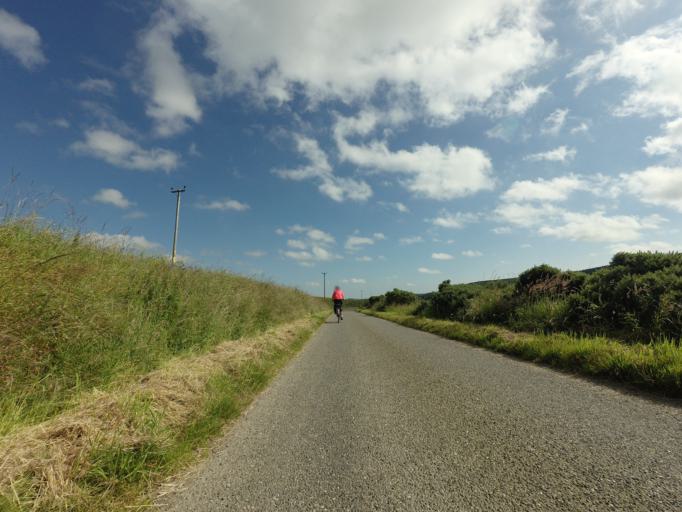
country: GB
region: Scotland
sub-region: Aberdeenshire
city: Turriff
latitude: 57.5801
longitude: -2.5057
